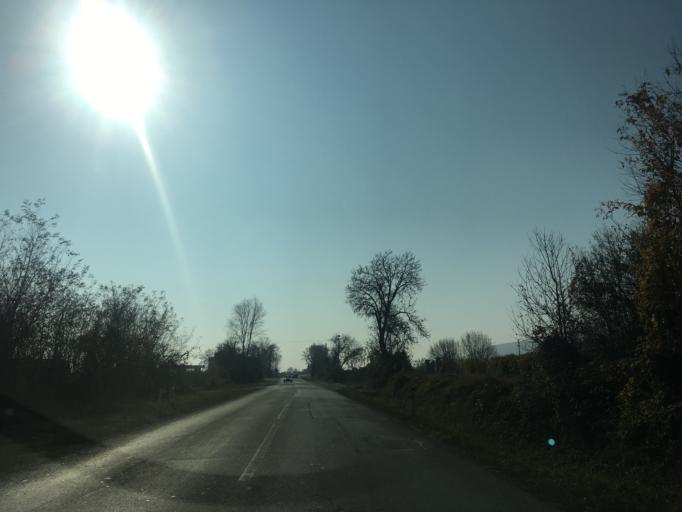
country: XK
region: Gjakova
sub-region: Komuna e Decanit
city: Strellc i Eperm
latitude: 42.6081
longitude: 20.3018
